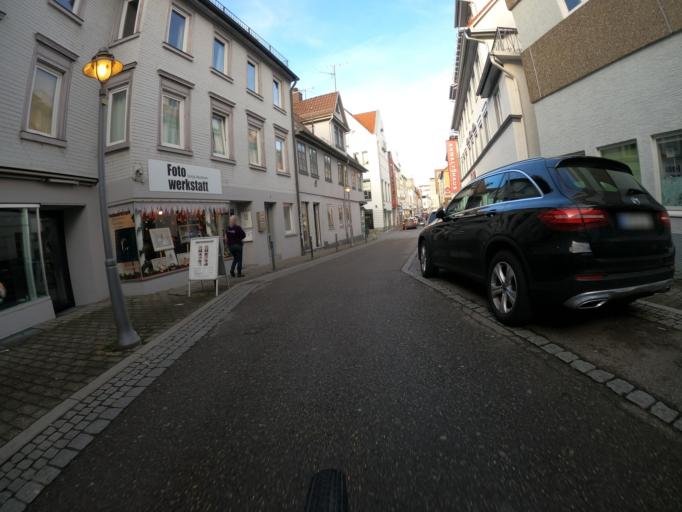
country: DE
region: Baden-Wuerttemberg
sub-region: Regierungsbezirk Stuttgart
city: Goeppingen
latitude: 48.7023
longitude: 9.6545
